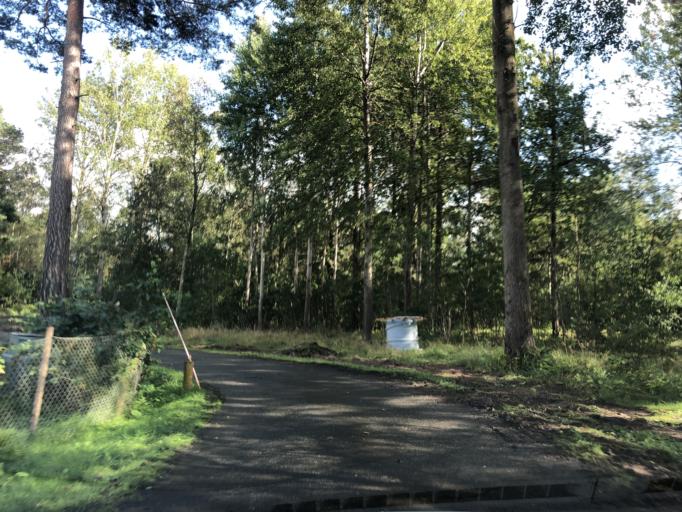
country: SE
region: Vaestra Goetaland
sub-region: Goteborg
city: Goeteborg
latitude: 57.7720
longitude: 11.9528
